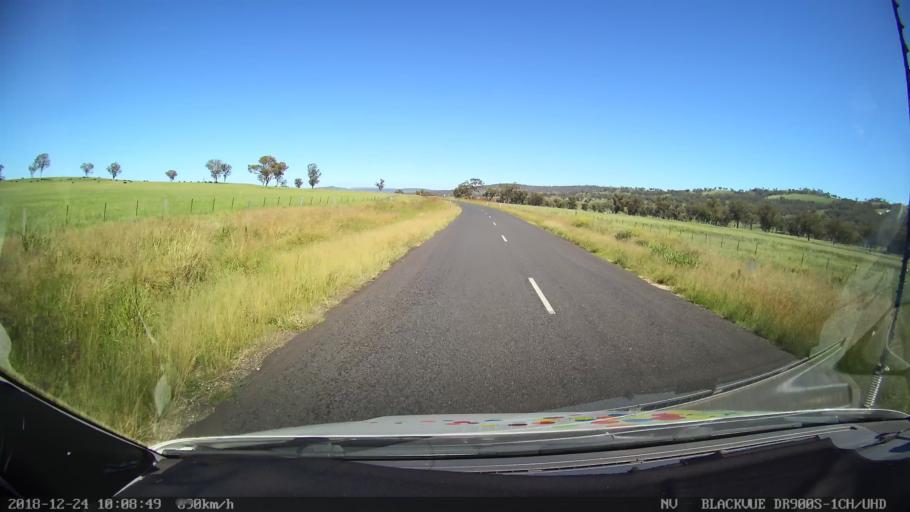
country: AU
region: New South Wales
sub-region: Liverpool Plains
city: Quirindi
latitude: -31.6652
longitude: 150.6995
